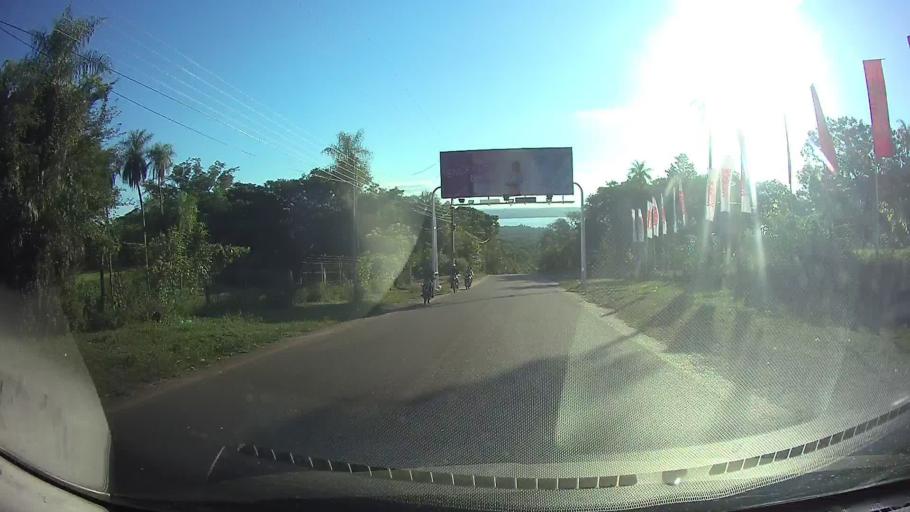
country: PY
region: Cordillera
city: San Bernardino
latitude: -25.3162
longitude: -57.2668
